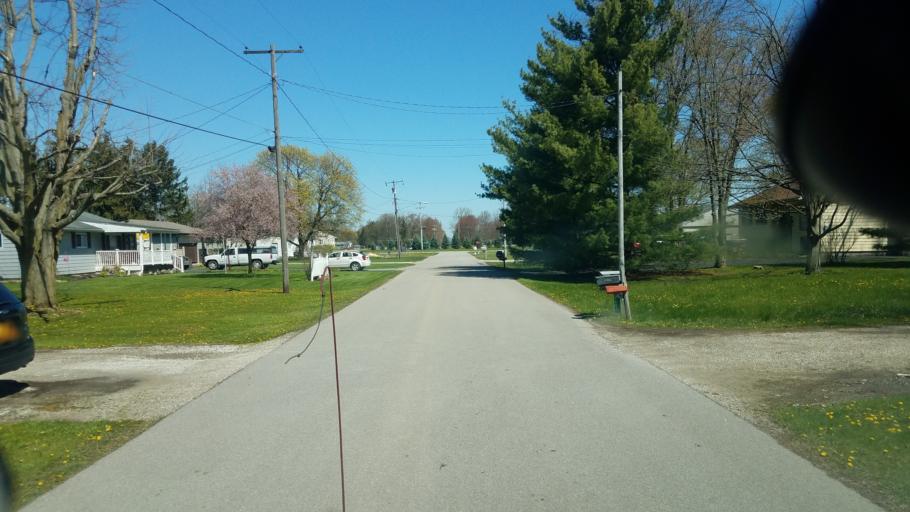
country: US
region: Ohio
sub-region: Marion County
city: Marion
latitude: 40.6410
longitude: -83.0772
